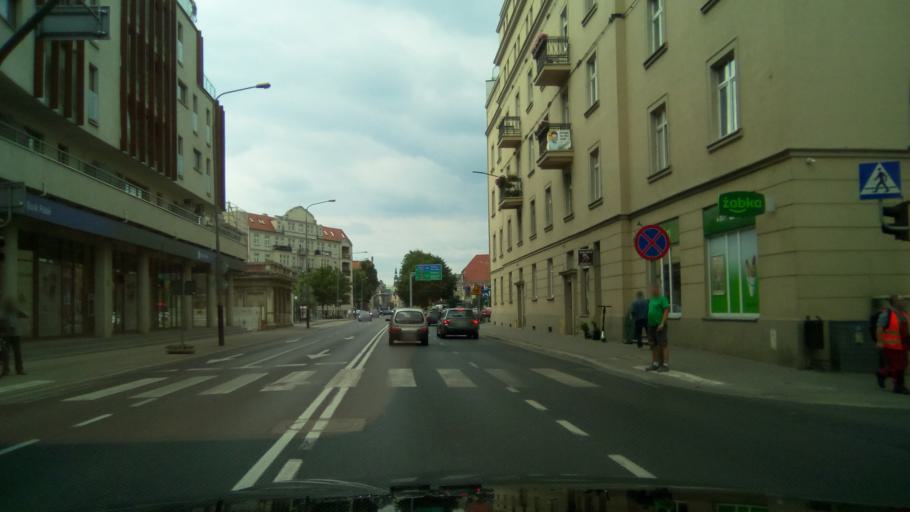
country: PL
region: Greater Poland Voivodeship
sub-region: Poznan
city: Poznan
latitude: 52.4128
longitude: 16.9389
